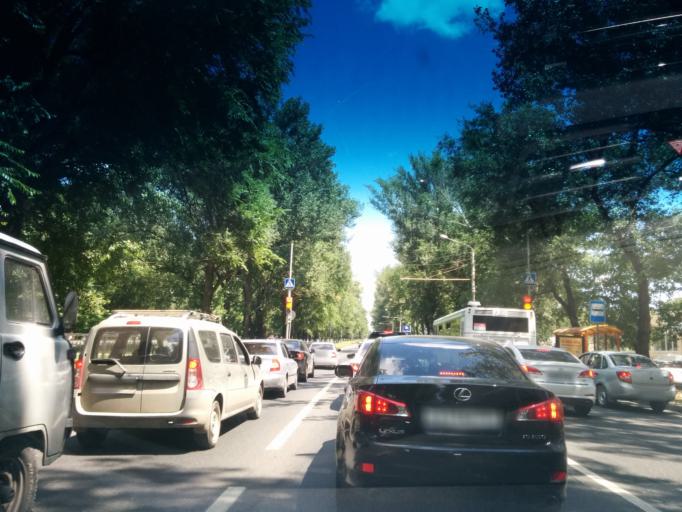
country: RU
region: Rostov
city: Aksay
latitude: 47.2624
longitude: 39.8096
